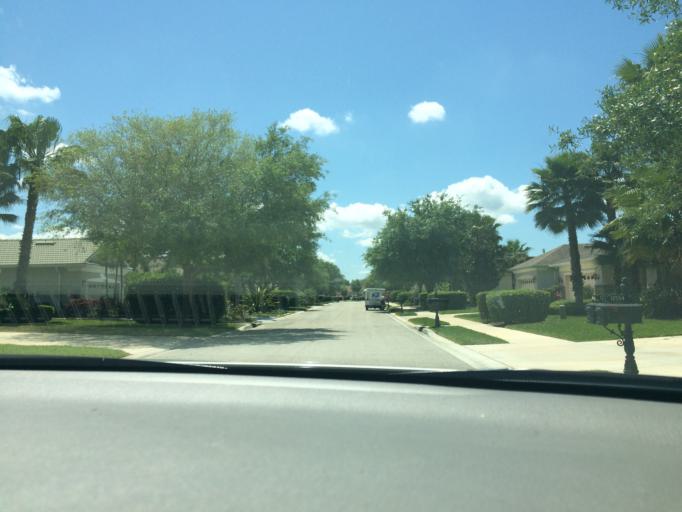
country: US
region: Florida
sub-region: Manatee County
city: Ellenton
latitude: 27.4980
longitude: -82.4167
